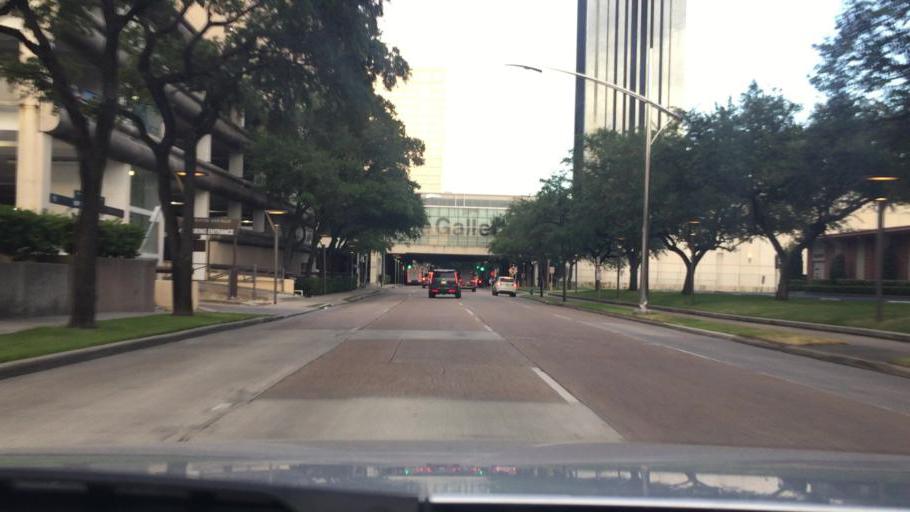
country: US
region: Texas
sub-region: Harris County
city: Bellaire
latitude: 29.7381
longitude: -95.4661
